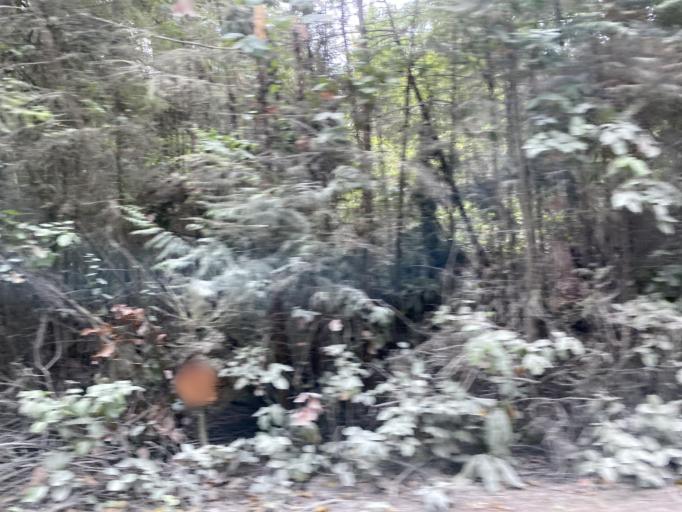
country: US
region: Washington
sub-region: Island County
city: Coupeville
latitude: 48.2112
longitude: -122.7294
